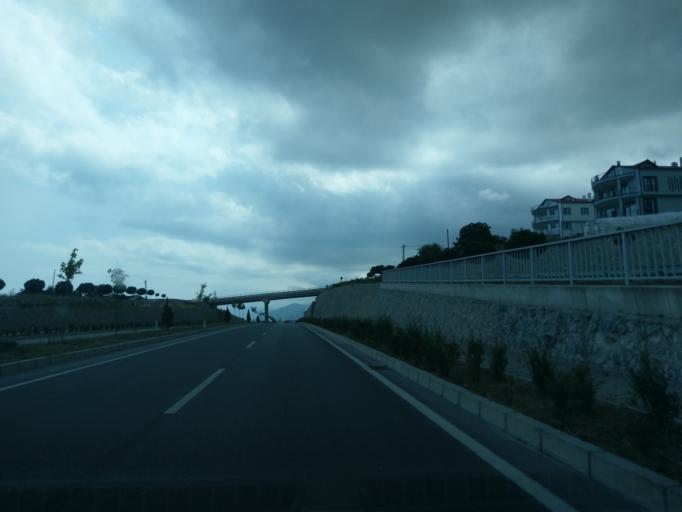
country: TR
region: Sinop
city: Gerze
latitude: 41.8027
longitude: 35.1769
